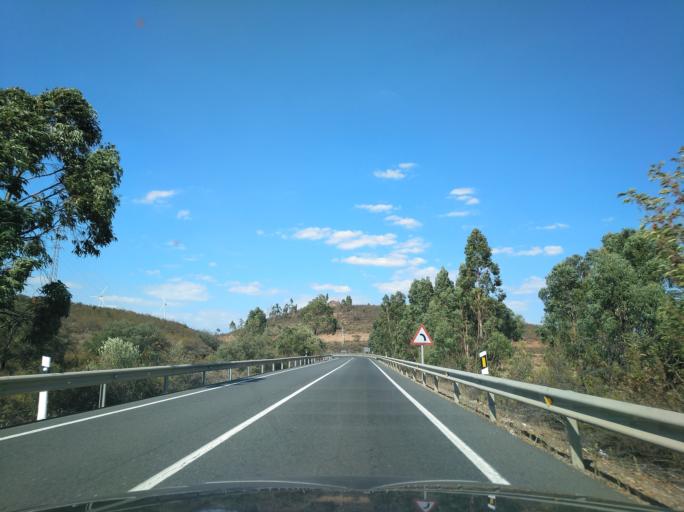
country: ES
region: Andalusia
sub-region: Provincia de Huelva
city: Alosno
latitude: 37.5766
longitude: -7.1138
